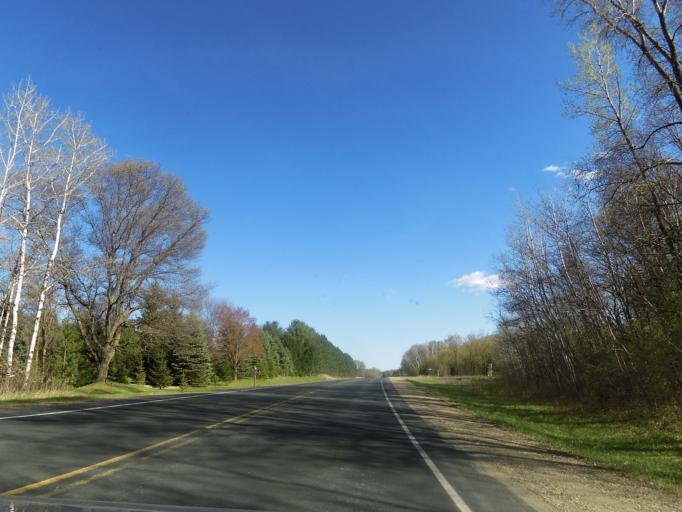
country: US
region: Minnesota
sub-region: Washington County
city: Bayport
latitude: 45.0560
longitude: -92.7267
